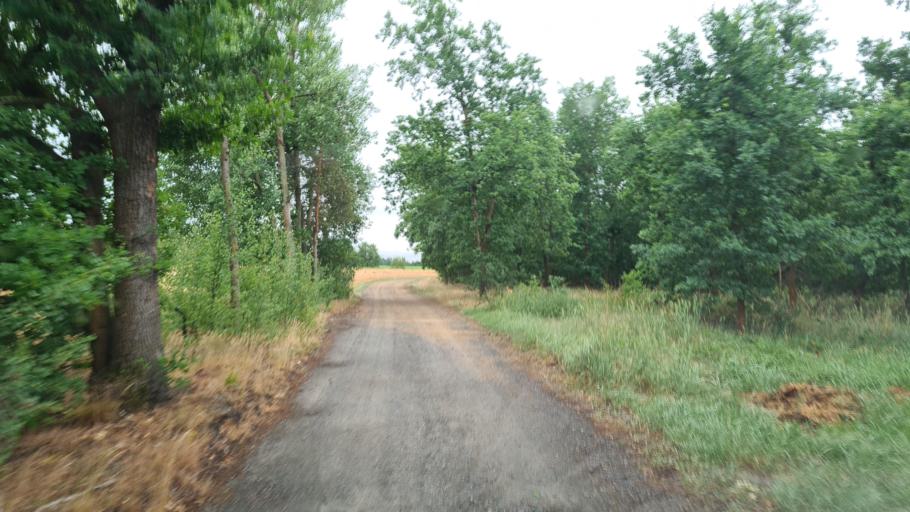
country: DE
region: Brandenburg
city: Bad Liebenwerda
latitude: 51.5026
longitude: 13.3164
